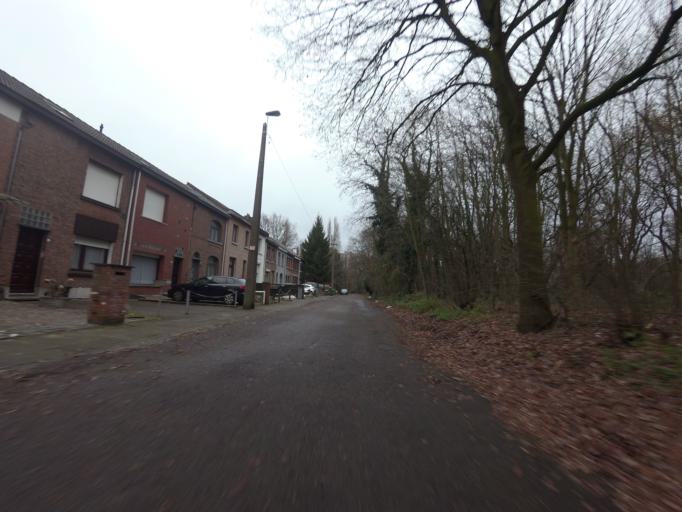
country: BE
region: Flanders
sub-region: Provincie Antwerpen
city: Hoboken
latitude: 51.1672
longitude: 4.3464
